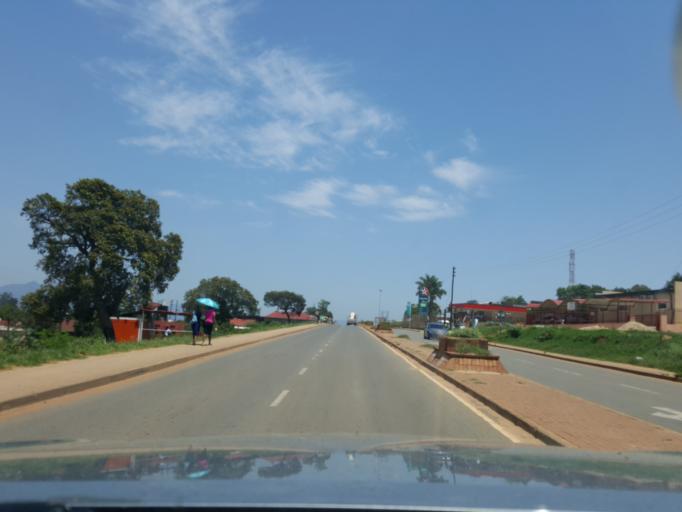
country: ZA
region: Limpopo
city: Thulamahashi
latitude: -24.8405
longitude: 31.0770
